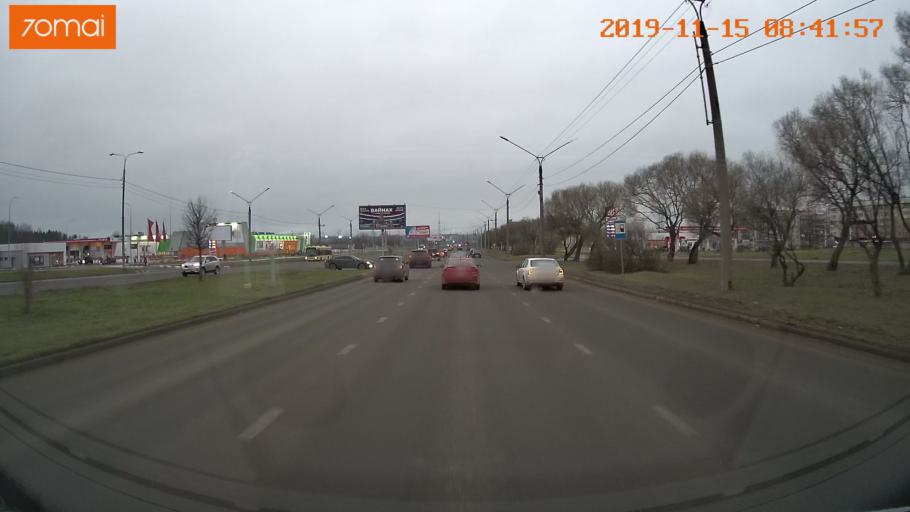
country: RU
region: Vologda
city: Cherepovets
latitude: 59.0993
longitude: 37.9105
